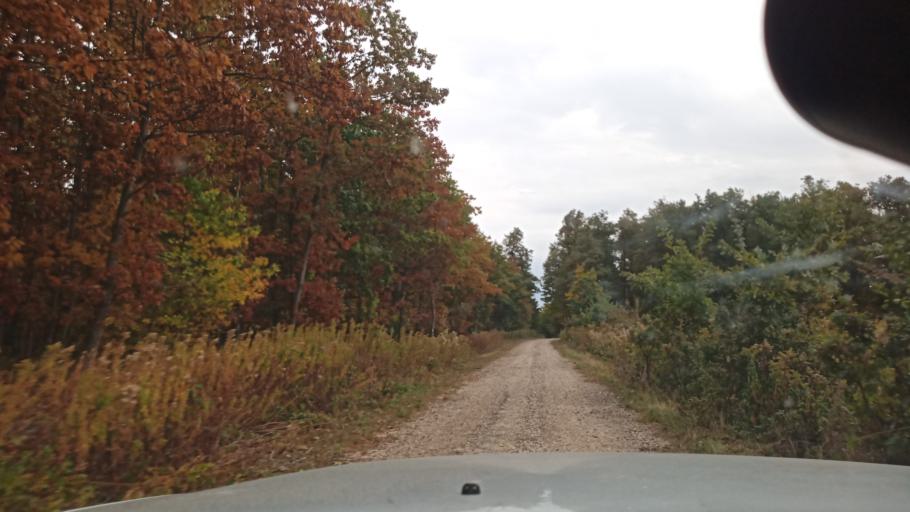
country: HU
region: Fejer
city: Bodajk
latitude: 47.3749
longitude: 18.2752
